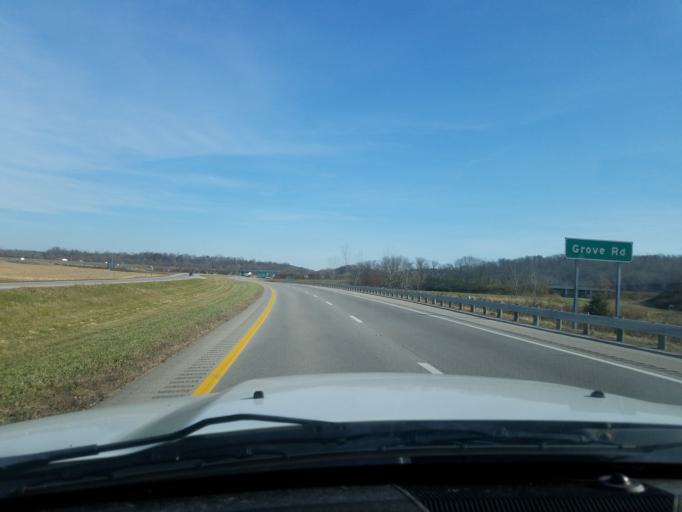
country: US
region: Ohio
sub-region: Pike County
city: Piketon
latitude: 39.0462
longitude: -83.0308
